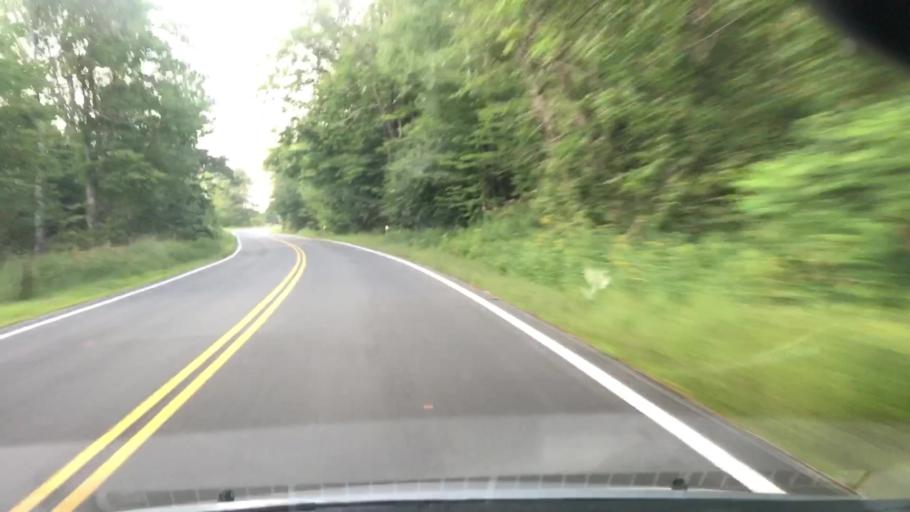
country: US
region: New Hampshire
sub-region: Grafton County
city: Woodsville
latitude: 44.2301
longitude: -72.0457
